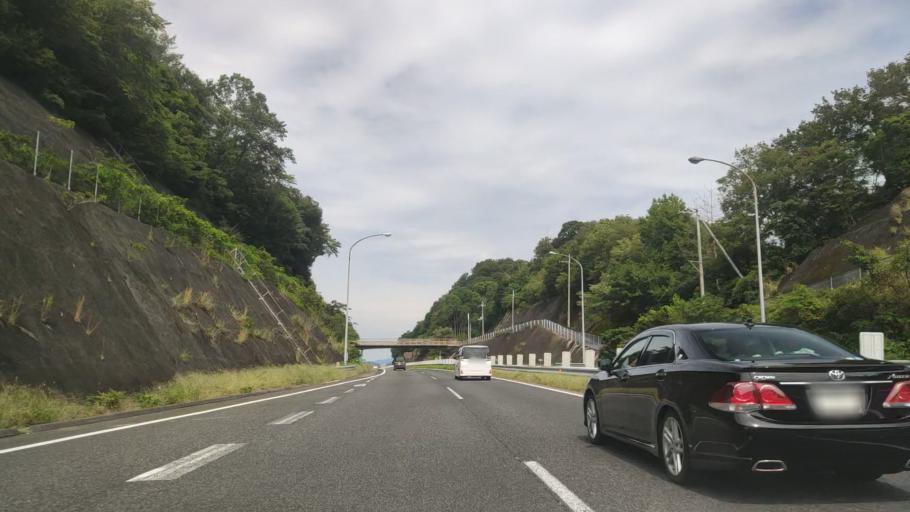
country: JP
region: Wakayama
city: Kainan
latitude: 34.1598
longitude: 135.2324
